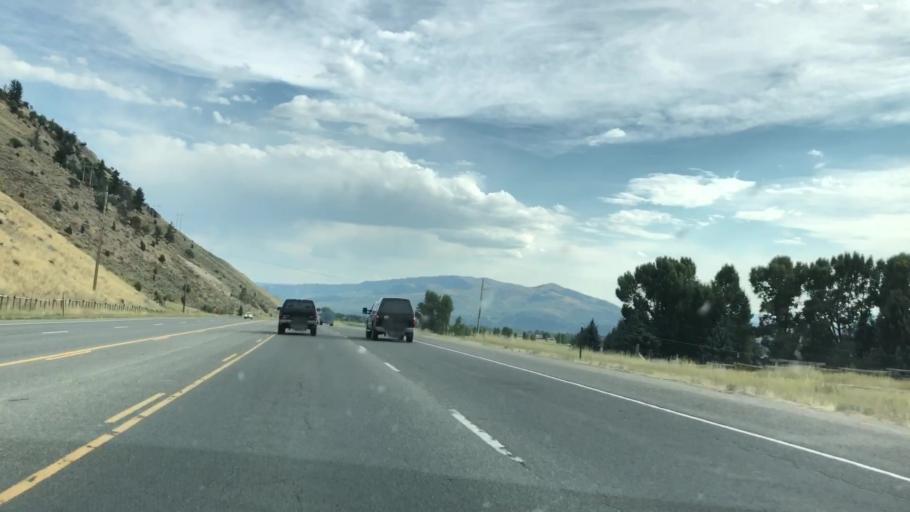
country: US
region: Wyoming
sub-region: Teton County
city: Rafter J Ranch
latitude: 43.4523
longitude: -110.7923
